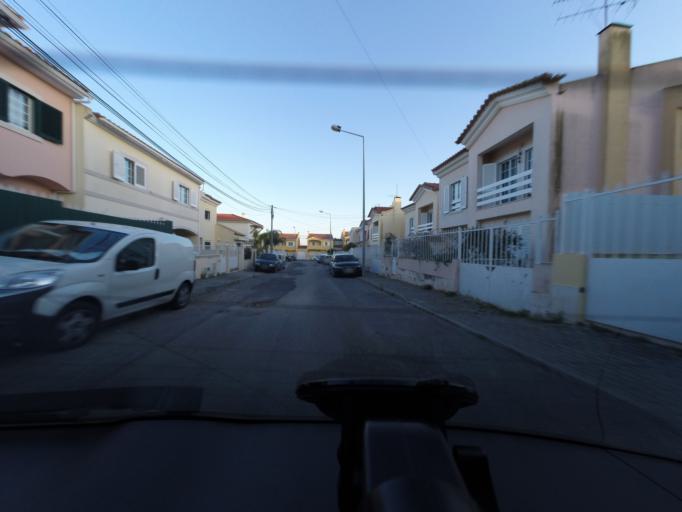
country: PT
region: Lisbon
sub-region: Sintra
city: Rio de Mouro
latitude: 38.7551
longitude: -9.3549
